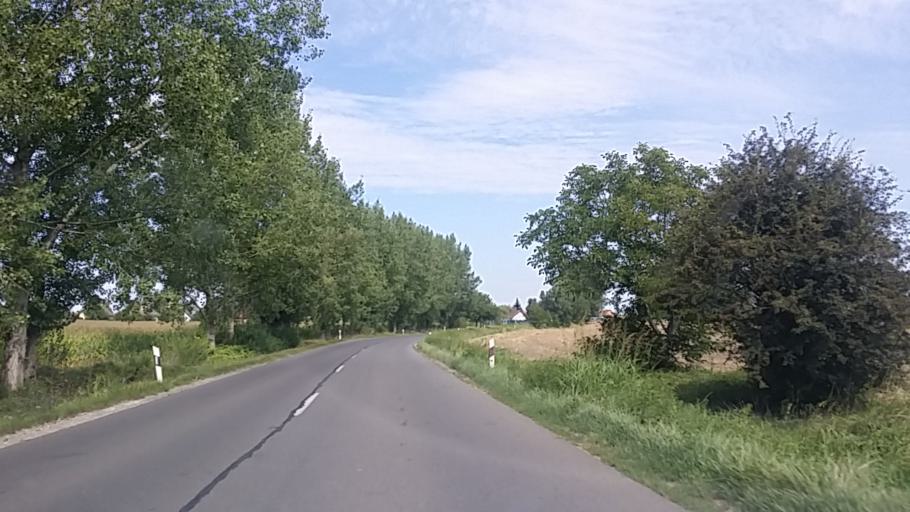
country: HU
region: Tolna
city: Dombovar
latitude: 46.3226
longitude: 18.1304
